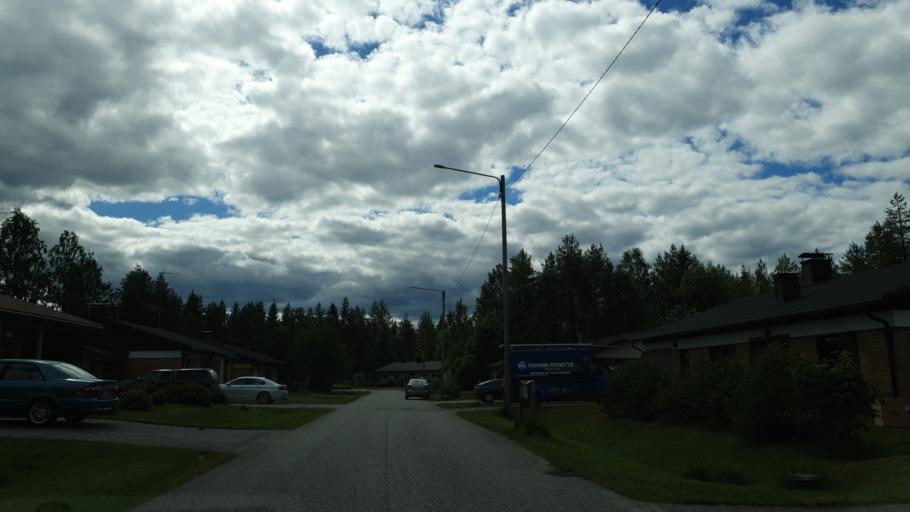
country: FI
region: Kainuu
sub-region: Kehys-Kainuu
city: Kuhmo
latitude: 64.1158
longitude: 29.4785
